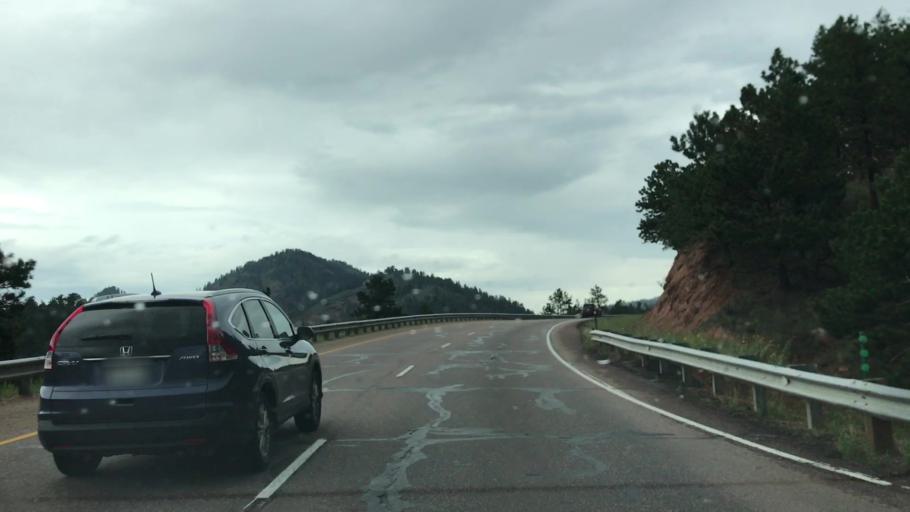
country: US
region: Colorado
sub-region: El Paso County
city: Cascade-Chipita Park
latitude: 38.9496
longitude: -105.0249
